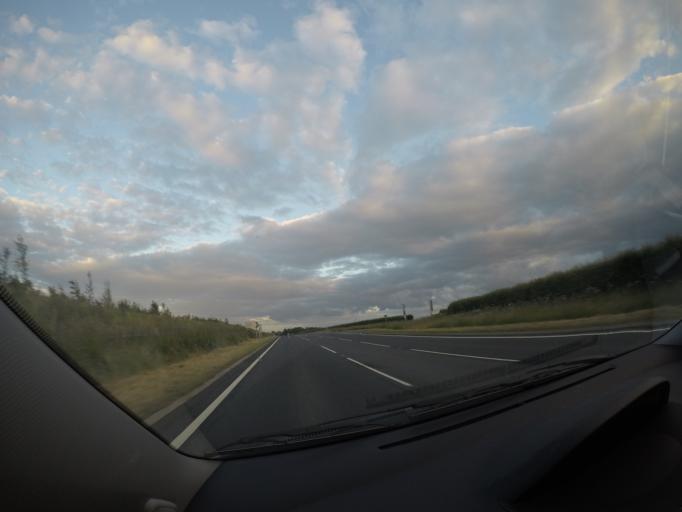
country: GB
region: England
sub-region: North Yorkshire
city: Bedale
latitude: 54.2621
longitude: -1.5182
